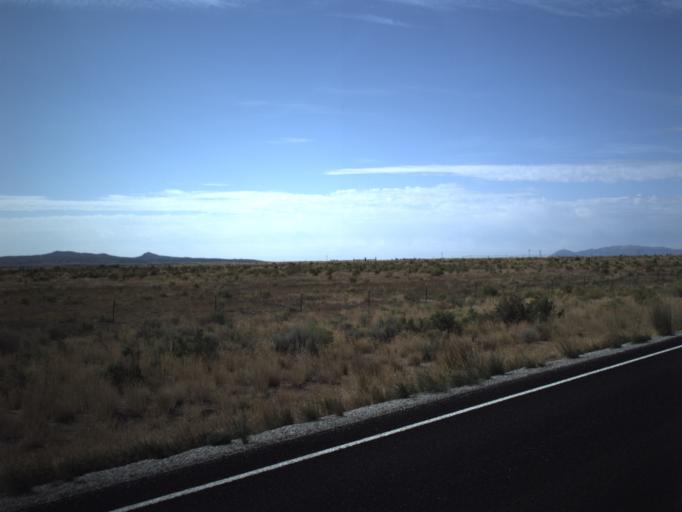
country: US
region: Idaho
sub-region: Cassia County
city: Burley
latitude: 41.7715
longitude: -113.5001
